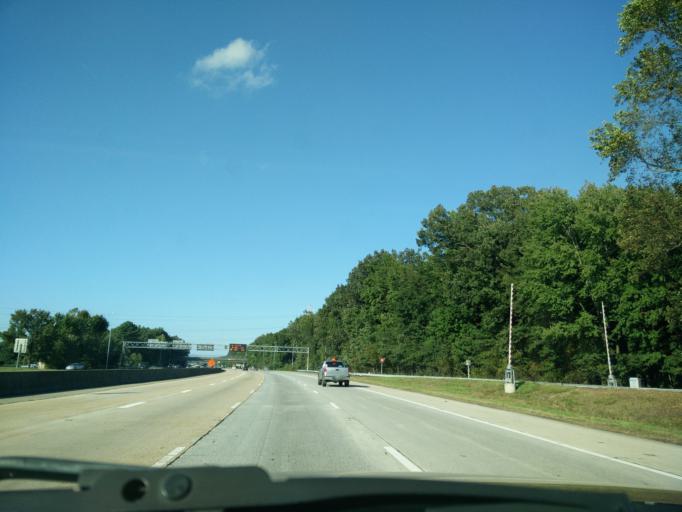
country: US
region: Virginia
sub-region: City of Chesapeake
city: Chesapeake
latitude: 36.8095
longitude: -76.1949
